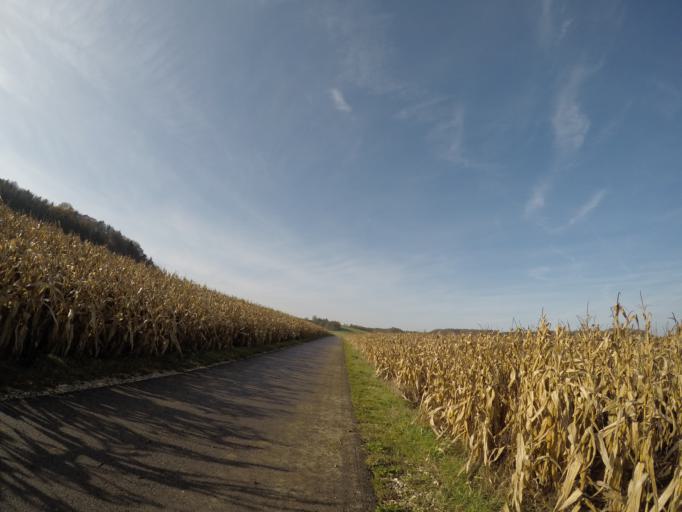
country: DE
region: Baden-Wuerttemberg
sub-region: Tuebingen Region
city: Bernstadt
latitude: 48.4871
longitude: 10.0088
